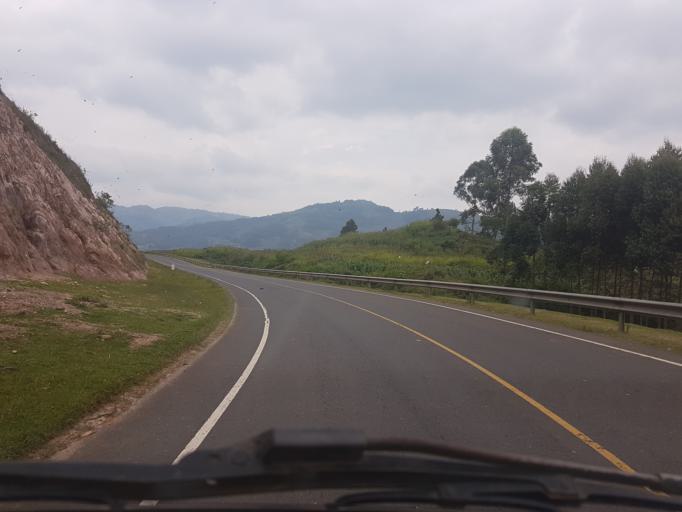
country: UG
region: Western Region
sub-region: Kabale District
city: Kabale
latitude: -1.2102
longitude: 29.8322
